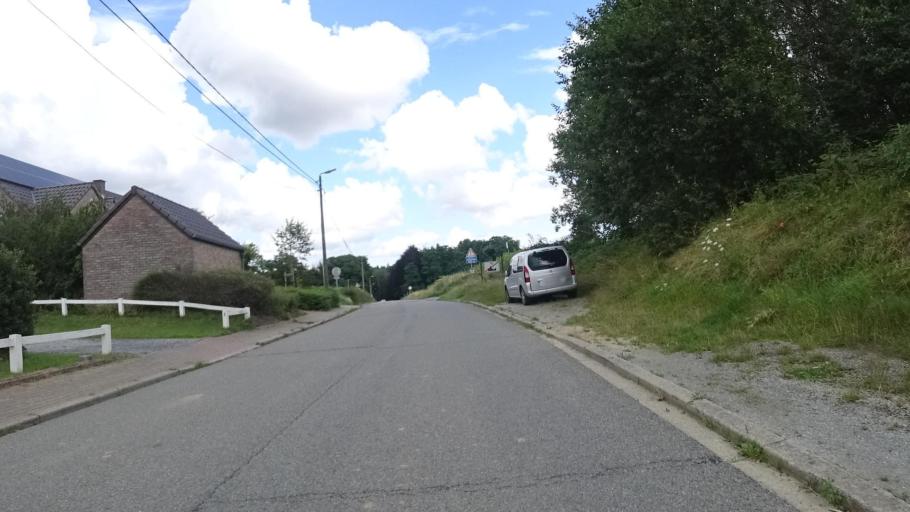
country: BE
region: Wallonia
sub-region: Province du Brabant Wallon
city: Villers-la-Ville
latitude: 50.5618
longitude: 4.5572
